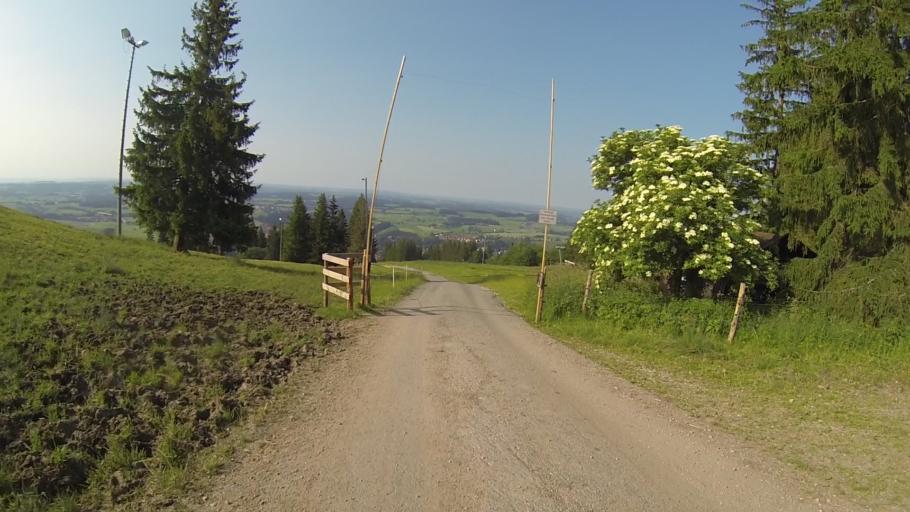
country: DE
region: Bavaria
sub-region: Swabia
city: Nesselwang
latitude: 47.6071
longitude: 10.4988
